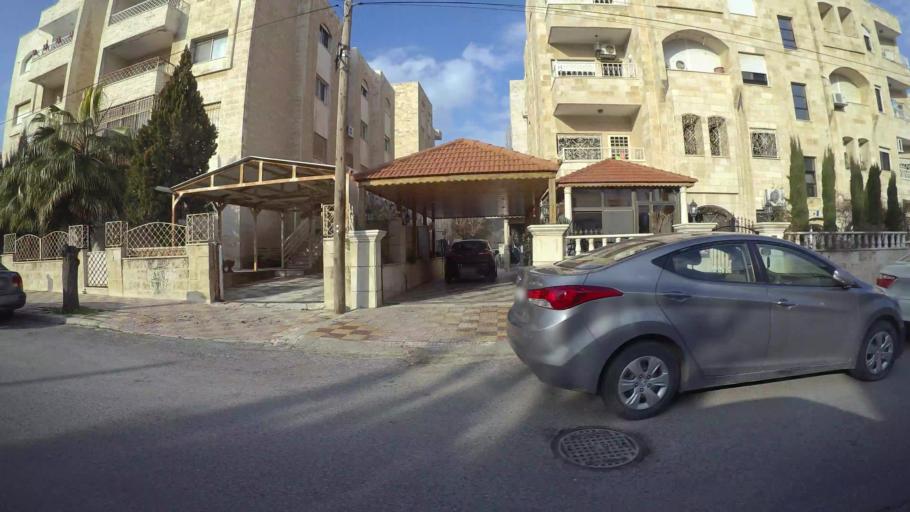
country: JO
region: Amman
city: Al Jubayhah
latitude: 31.9836
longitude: 35.8580
